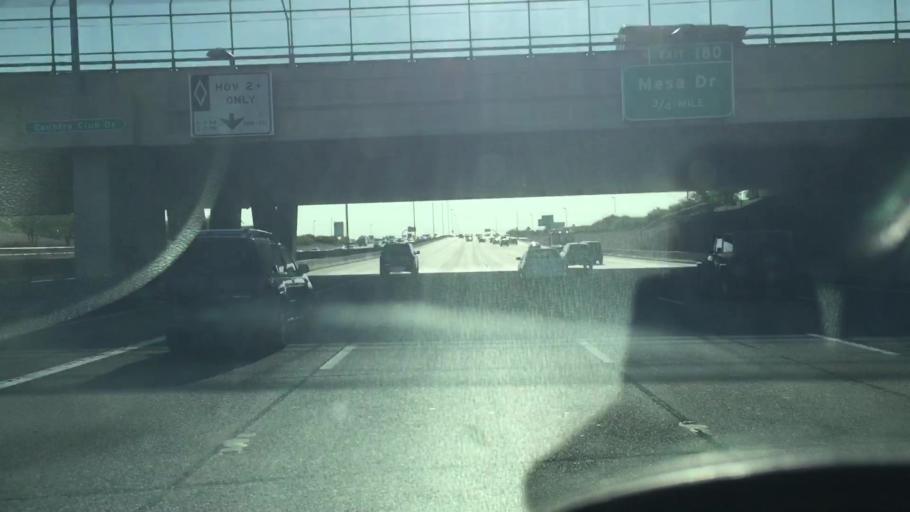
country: US
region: Arizona
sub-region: Maricopa County
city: San Carlos
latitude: 33.3853
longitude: -111.8415
